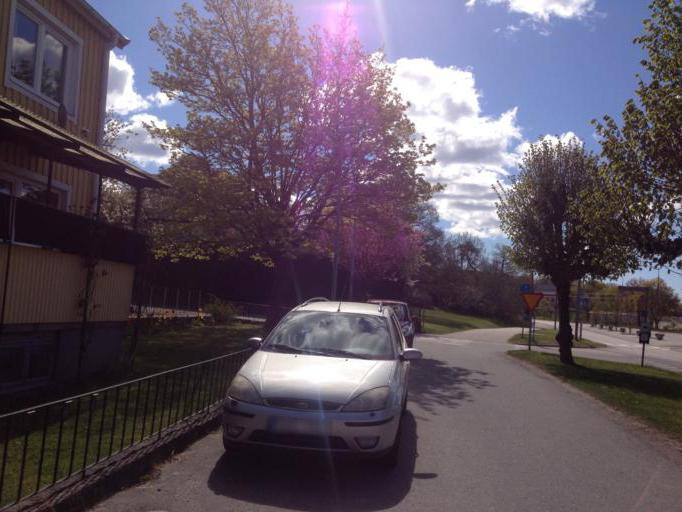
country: SE
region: Blekinge
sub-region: Ronneby Kommun
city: Ronneby
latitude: 56.2047
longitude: 15.2889
